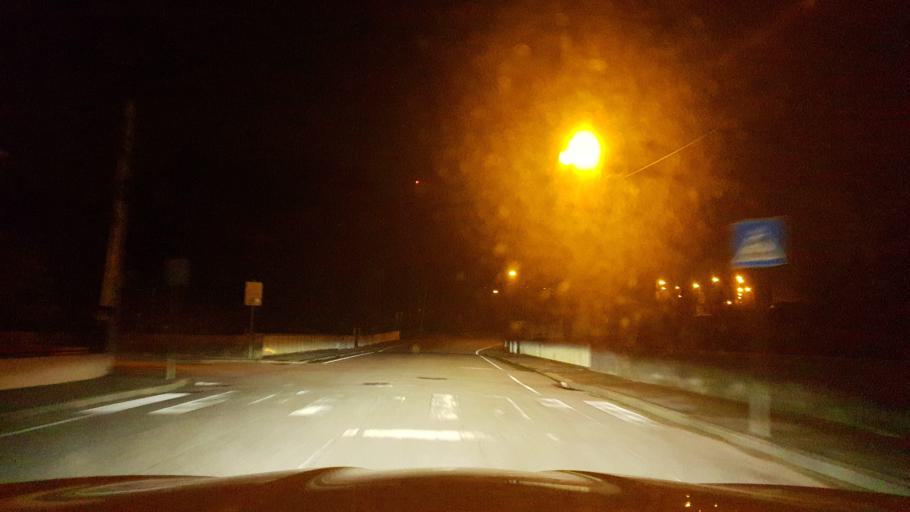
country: PT
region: Porto
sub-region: Matosinhos
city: Guifoes
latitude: 41.2173
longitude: -8.6587
